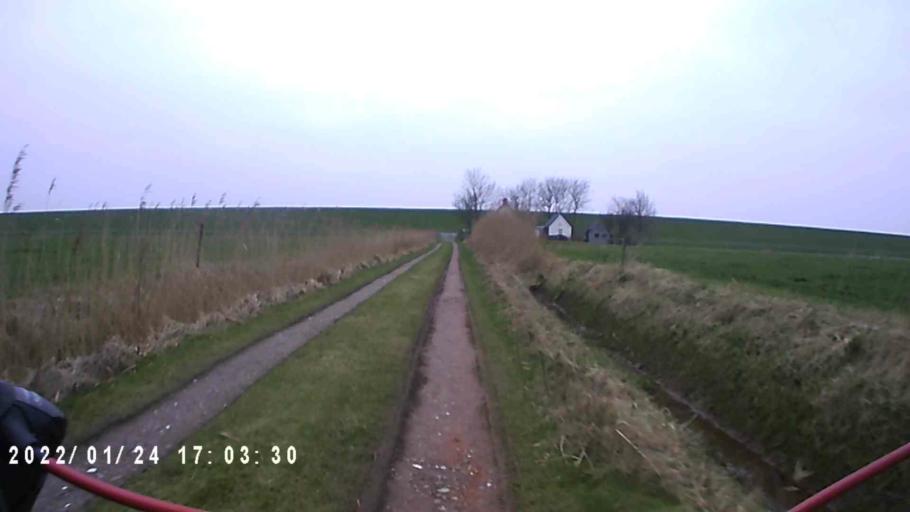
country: NL
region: Groningen
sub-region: Gemeente De Marne
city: Ulrum
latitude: 53.3936
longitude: 6.3195
